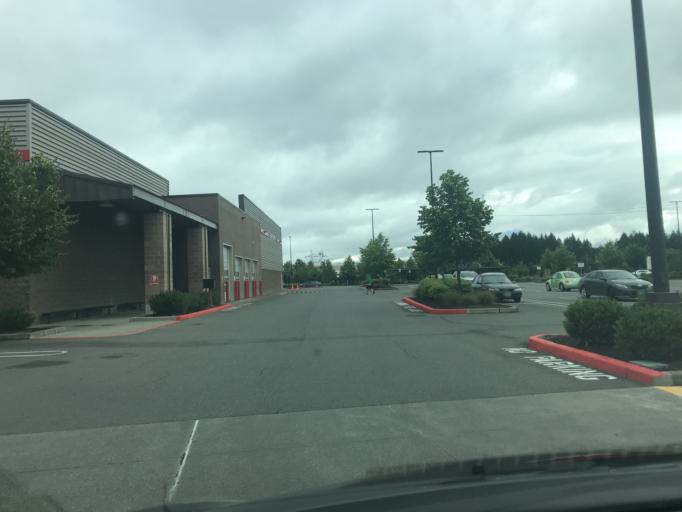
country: US
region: Washington
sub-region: King County
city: Covington
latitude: 47.3545
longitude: -122.1219
